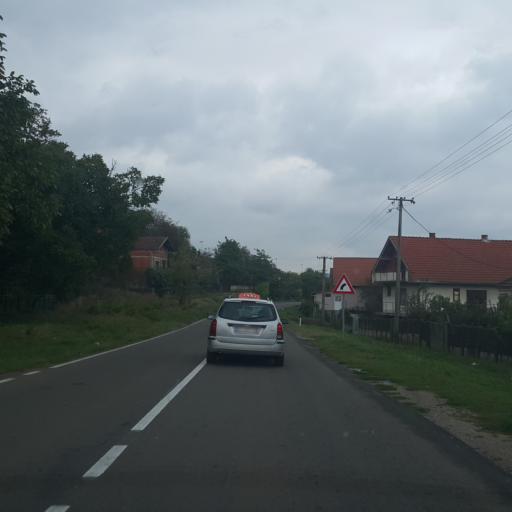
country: RS
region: Central Serbia
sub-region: Nisavski Okrug
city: Aleksinac
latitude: 43.5757
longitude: 21.6672
